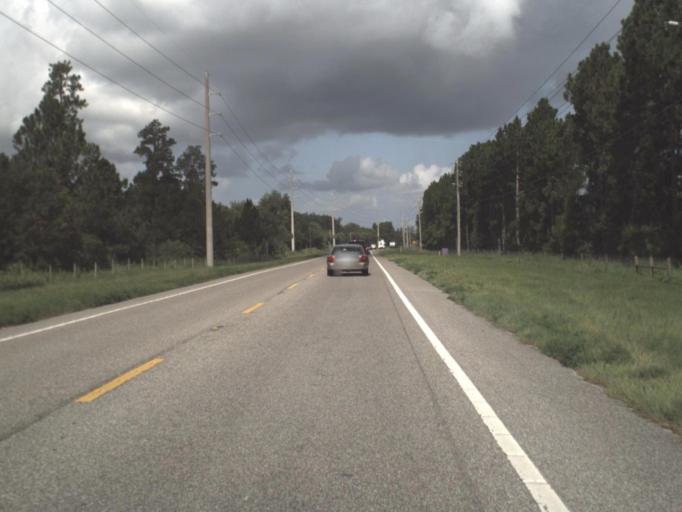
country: US
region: Florida
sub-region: Pasco County
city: Land O' Lakes
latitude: 28.3217
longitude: -82.4474
